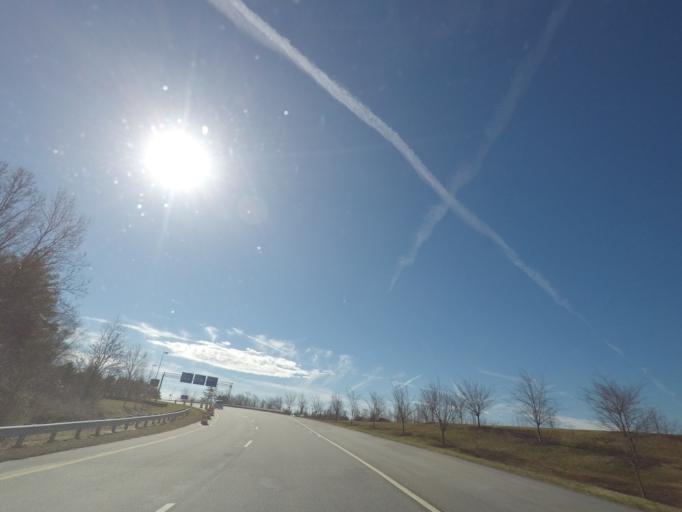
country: US
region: North Carolina
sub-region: Guilford County
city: Oak Ridge
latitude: 36.1057
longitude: -79.9443
